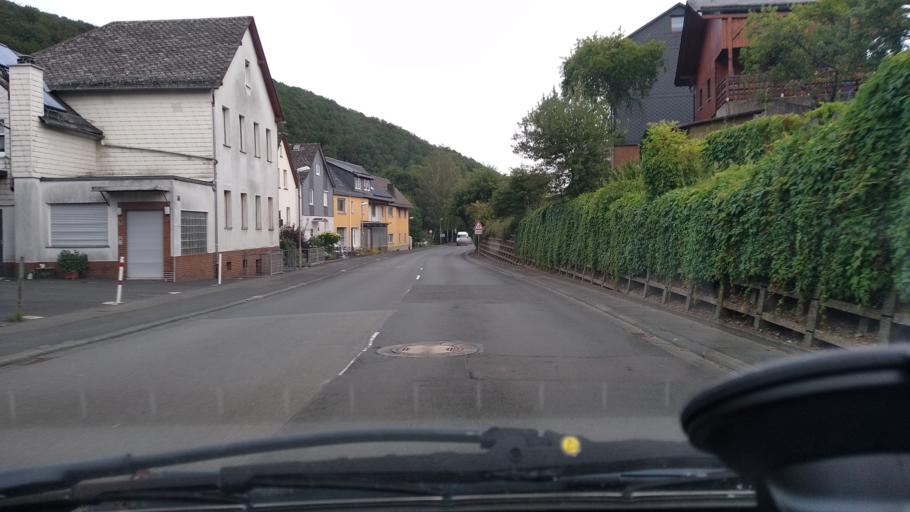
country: DE
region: Hesse
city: Dillenburg
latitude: 50.8444
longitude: 8.2847
